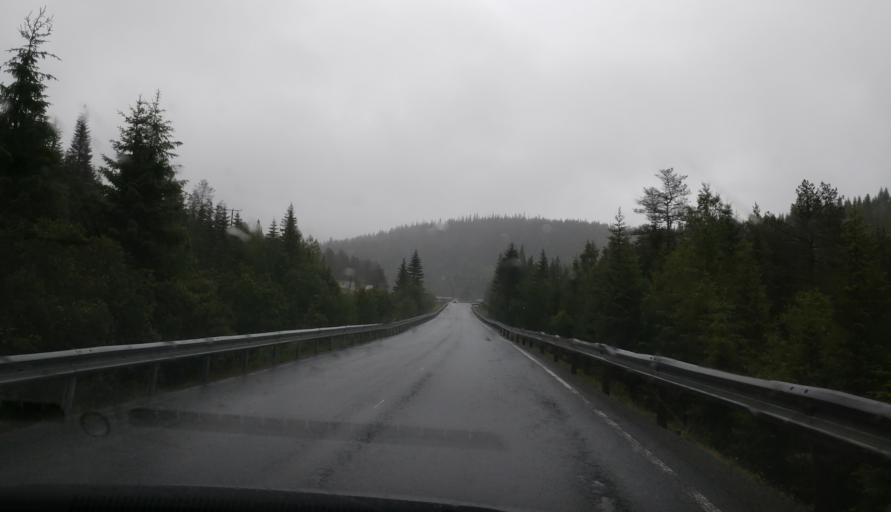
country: NO
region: Sor-Trondelag
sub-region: Selbu
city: Mebonden
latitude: 63.3384
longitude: 11.0842
